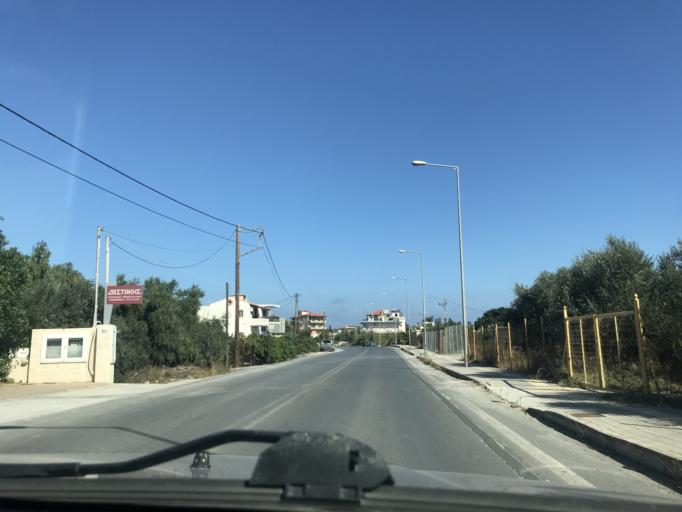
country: GR
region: Crete
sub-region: Nomos Irakleiou
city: Gazi
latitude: 35.3295
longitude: 25.0642
